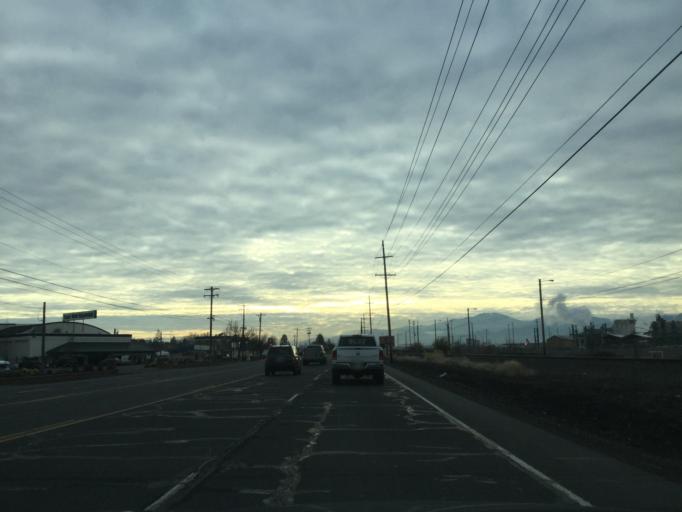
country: US
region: Oregon
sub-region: Jackson County
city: Central Point
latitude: 42.3613
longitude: -122.9068
